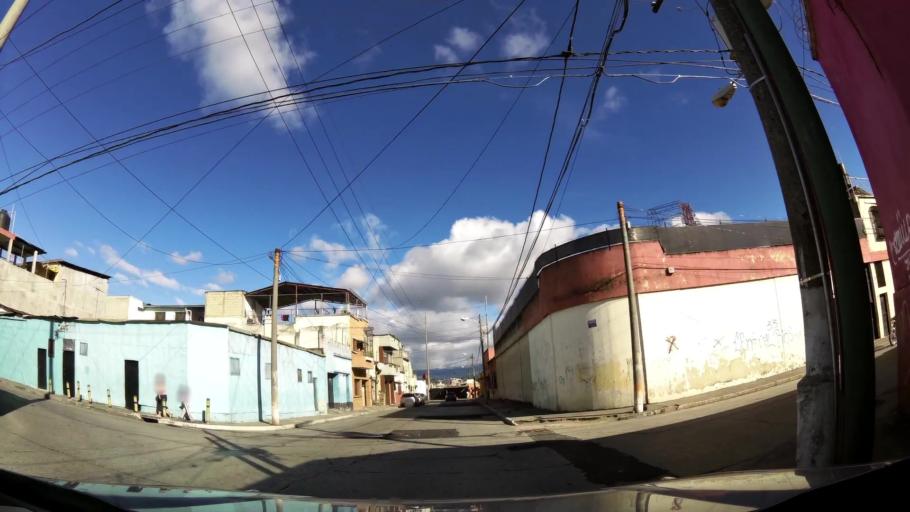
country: GT
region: Guatemala
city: Guatemala City
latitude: 14.6274
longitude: -90.5083
